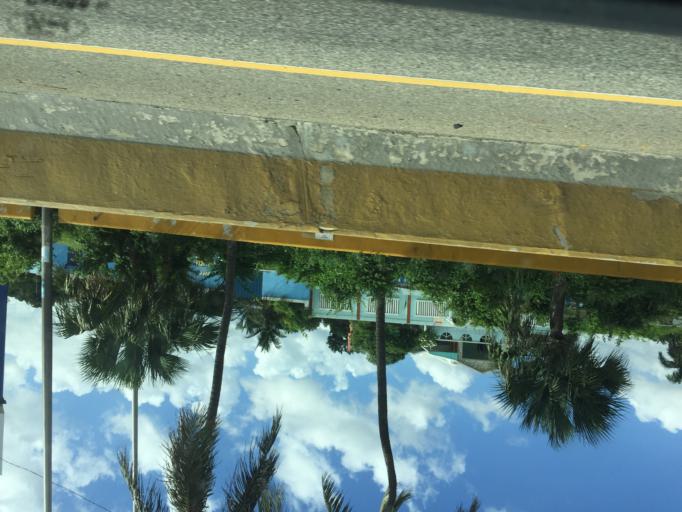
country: DO
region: Santo Domingo
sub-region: Santo Domingo
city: Santo Domingo Este
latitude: 18.4769
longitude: -69.8358
